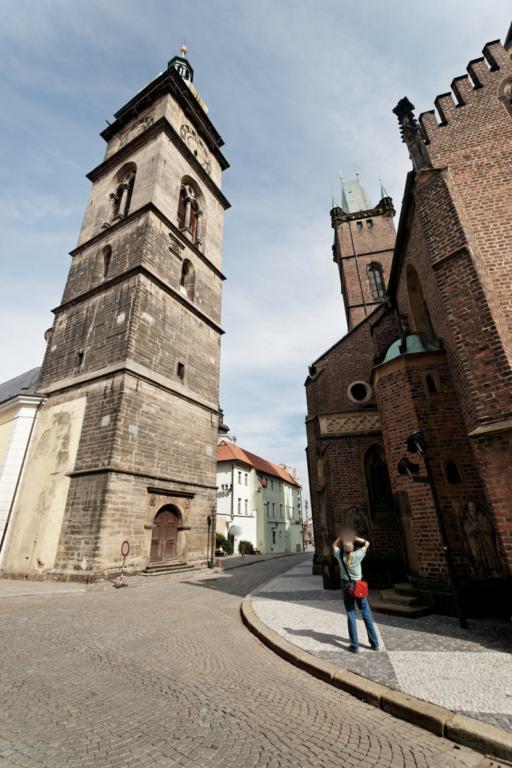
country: CZ
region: Kralovehradecky
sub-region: Okres Hradec Kralove
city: Hradec Kralove
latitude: 50.2088
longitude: 15.8306
